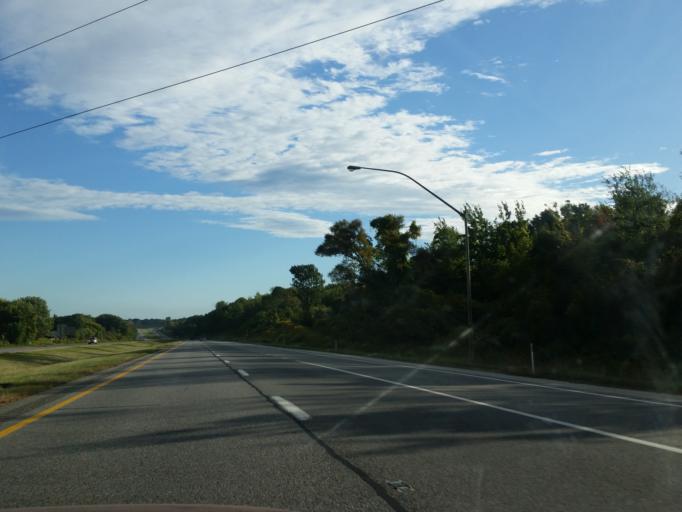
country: US
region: Pennsylvania
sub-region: Erie County
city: North East
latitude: 42.1907
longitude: -79.8263
